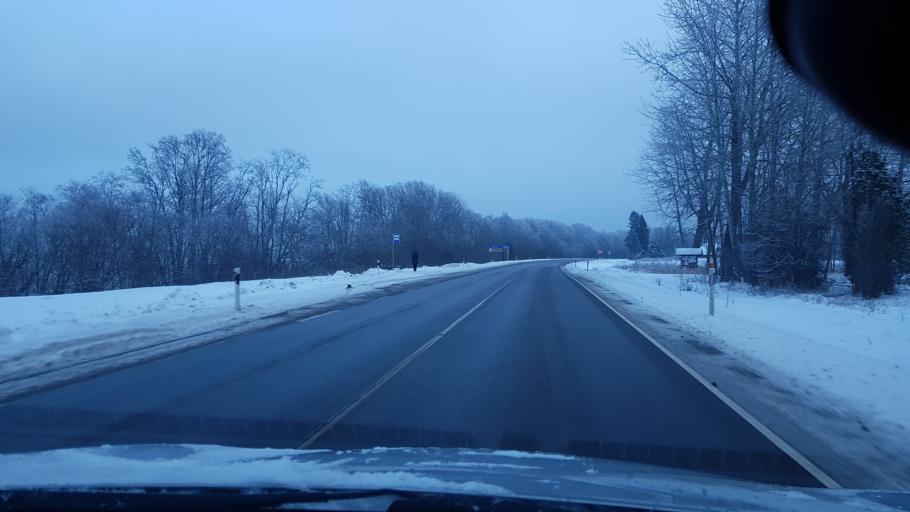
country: EE
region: Harju
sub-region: Paldiski linn
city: Paldiski
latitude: 59.3432
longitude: 24.1931
